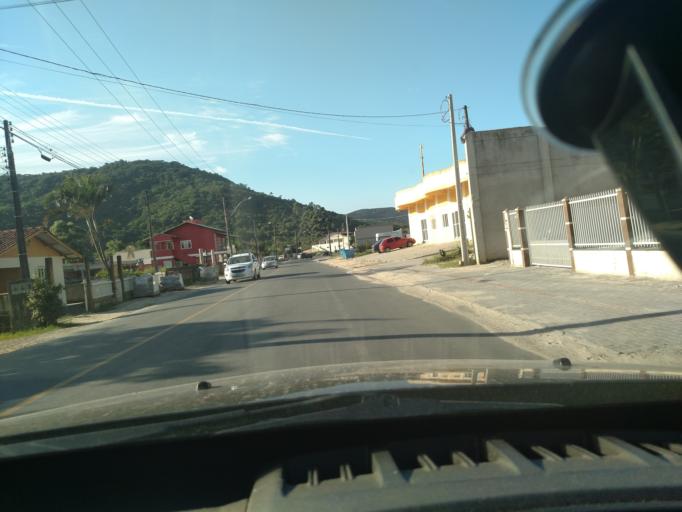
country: BR
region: Santa Catarina
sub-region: Porto Belo
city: Porto Belo
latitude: -27.1656
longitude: -48.5194
